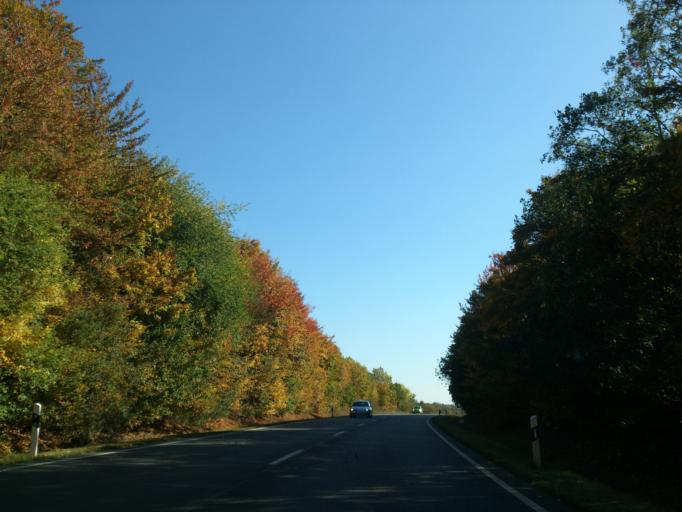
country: DE
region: Hesse
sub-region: Regierungsbezirk Kassel
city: Calden
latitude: 51.4265
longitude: 9.3569
